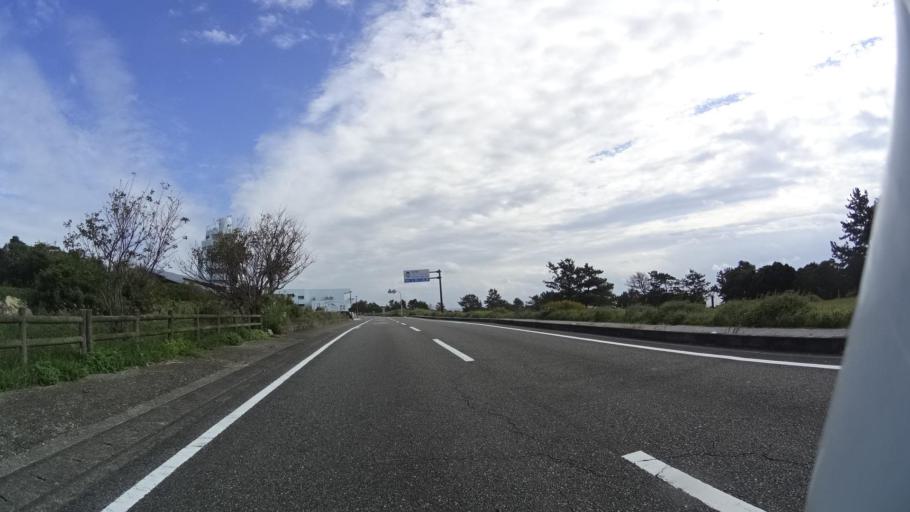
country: JP
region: Wakayama
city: Shingu
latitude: 33.4374
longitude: 135.7597
